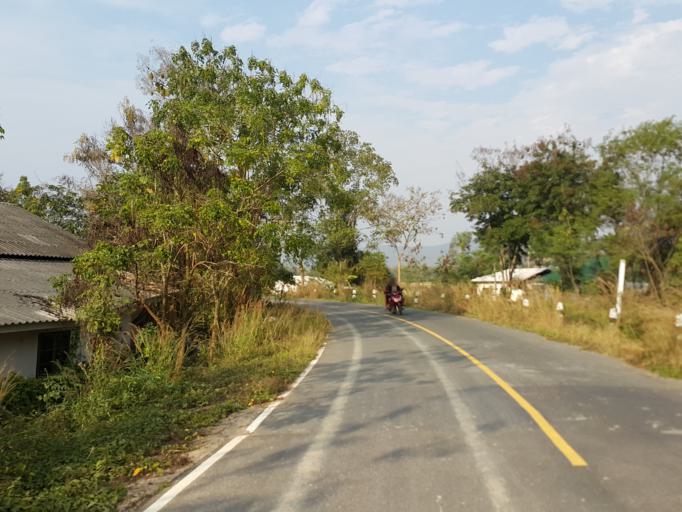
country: TH
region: Chiang Mai
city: San Sai
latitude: 18.8576
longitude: 99.1578
